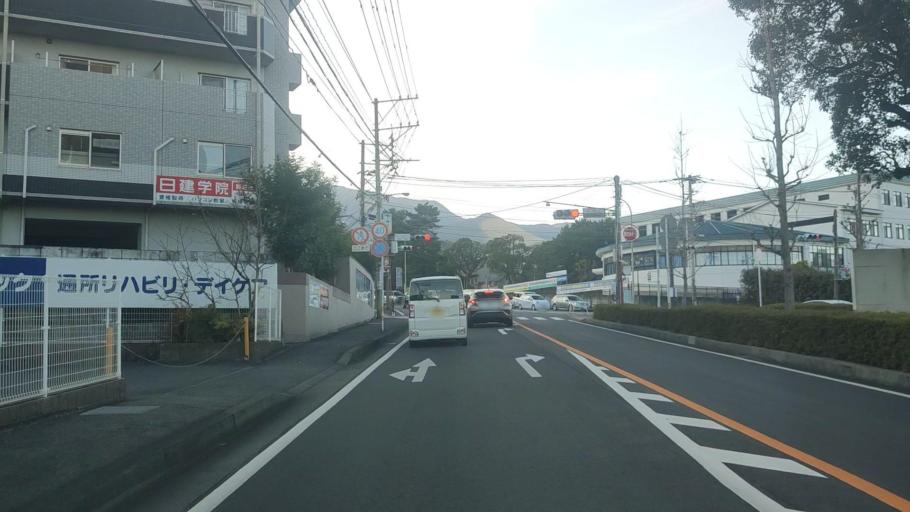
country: JP
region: Oita
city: Beppu
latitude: 33.2830
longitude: 131.4855
